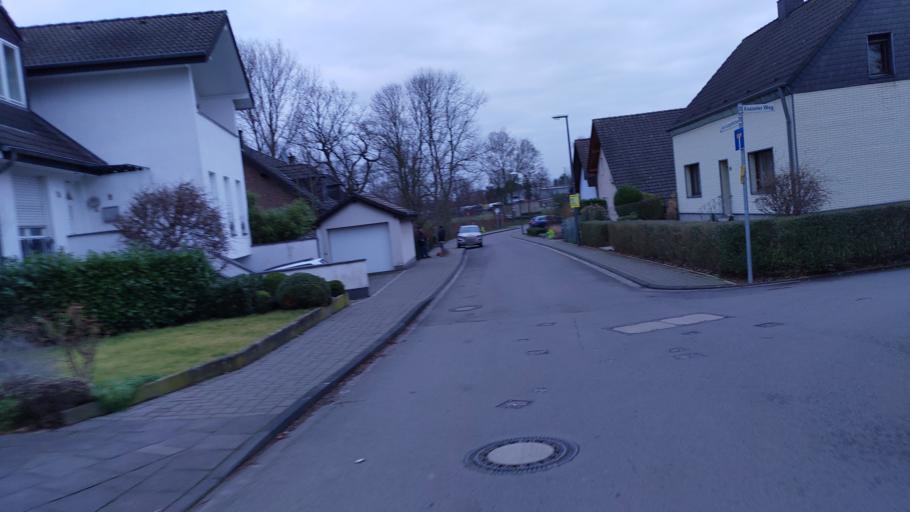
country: DE
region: North Rhine-Westphalia
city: Monheim am Rhein
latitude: 51.0375
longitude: 6.9074
